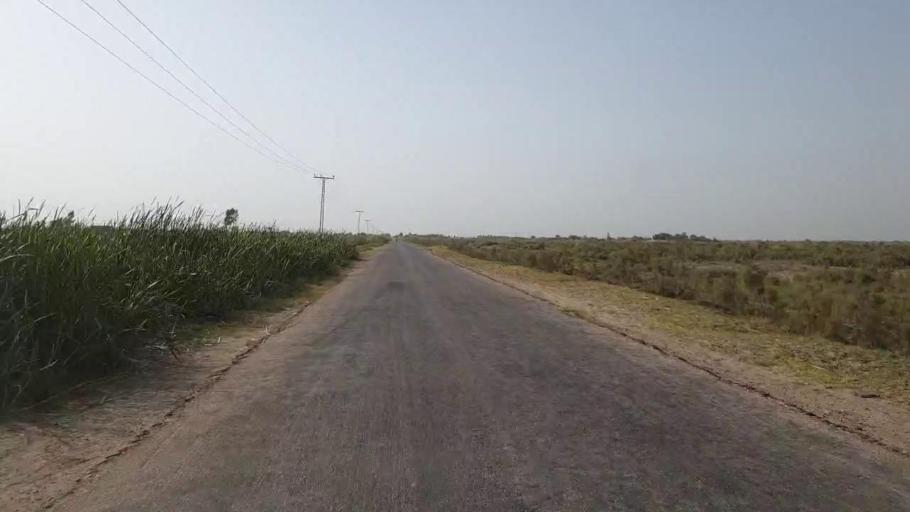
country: PK
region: Sindh
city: Khadro
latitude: 26.3487
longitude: 68.9235
